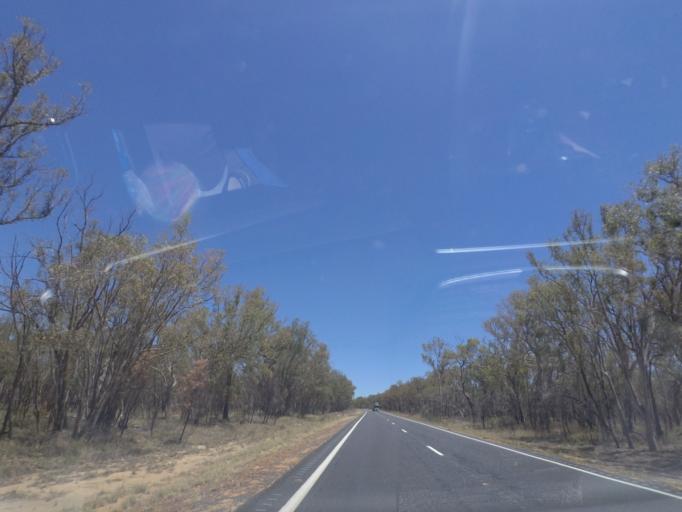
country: AU
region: New South Wales
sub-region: Warrumbungle Shire
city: Coonabarabran
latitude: -31.1756
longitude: 149.3581
